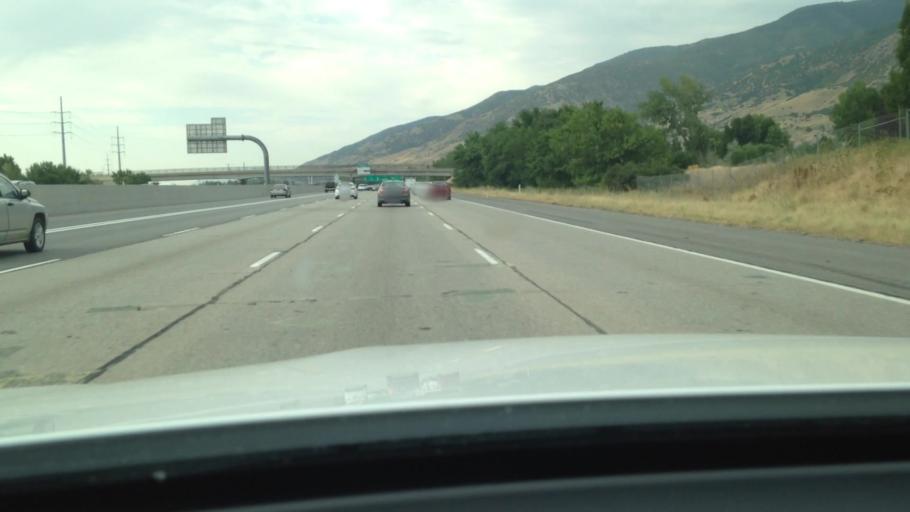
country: US
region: Utah
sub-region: Davis County
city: Farmington
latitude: 40.9617
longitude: -111.8910
